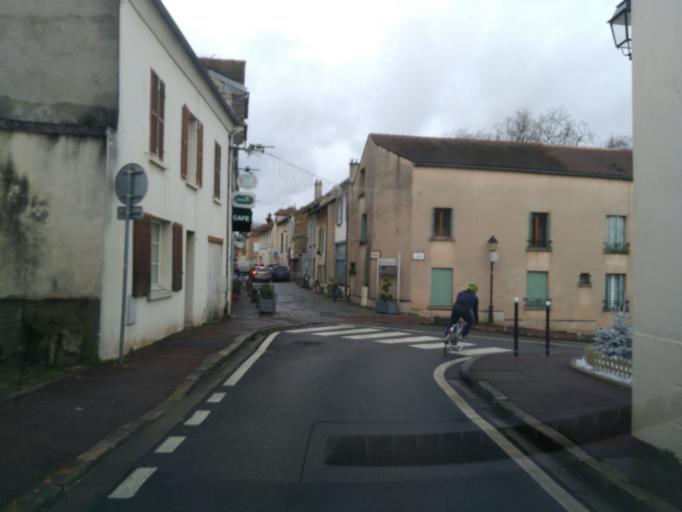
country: FR
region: Ile-de-France
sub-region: Departement des Yvelines
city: Chambourcy
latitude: 48.9059
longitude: 2.0387
